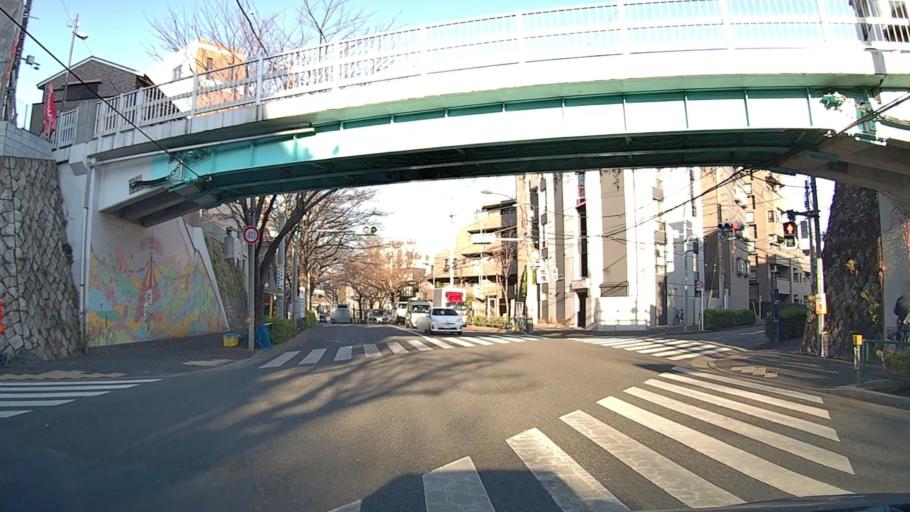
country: JP
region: Tokyo
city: Tokyo
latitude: 35.7205
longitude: 139.6710
